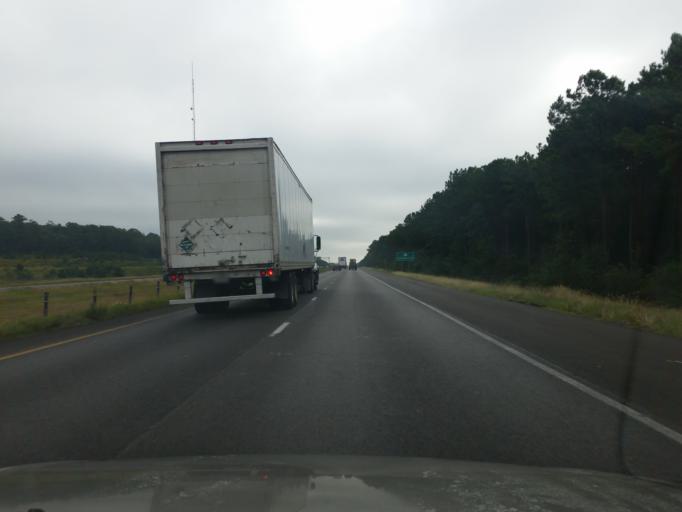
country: US
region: Alabama
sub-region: Baldwin County
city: Spanish Fort
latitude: 30.6573
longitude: -87.8993
